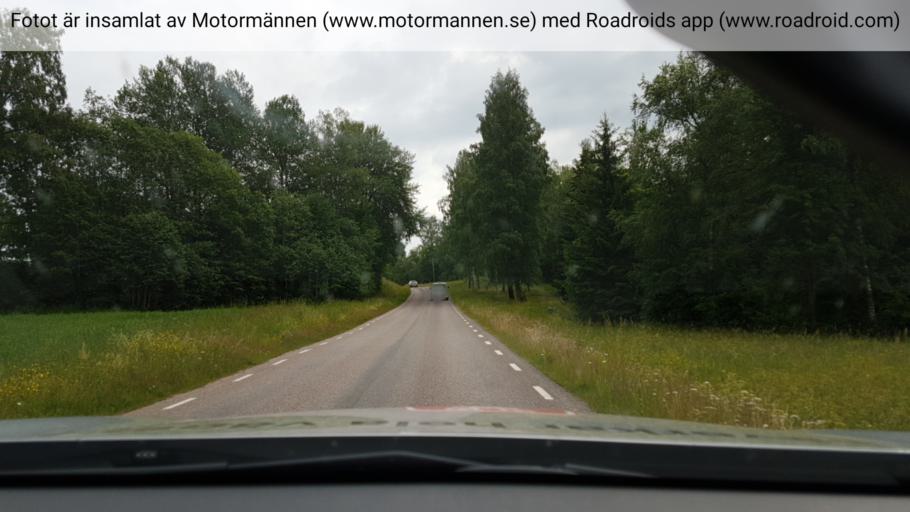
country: SE
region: Vaestra Goetaland
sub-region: Tidaholms Kommun
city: Tidaholm
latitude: 58.0701
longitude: 13.9337
